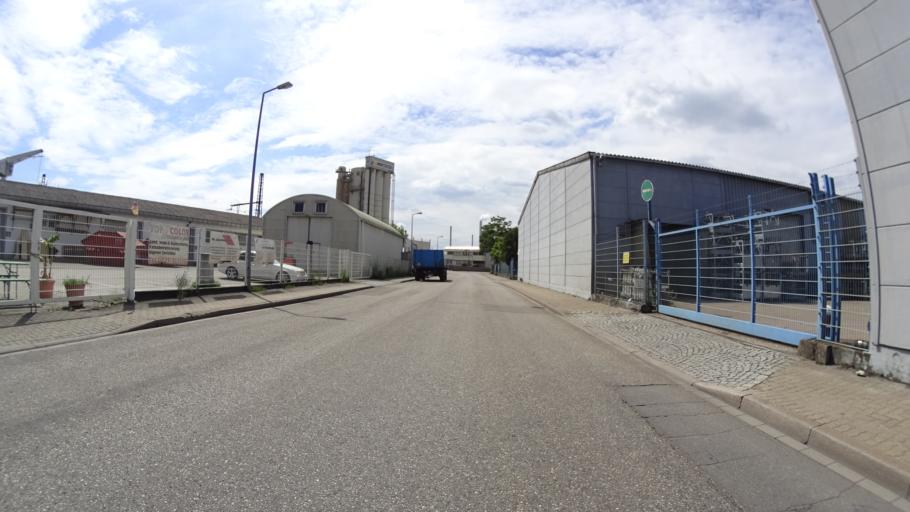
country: DE
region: Baden-Wuerttemberg
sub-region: Karlsruhe Region
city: Rheinstetten
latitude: 49.0120
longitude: 8.3349
